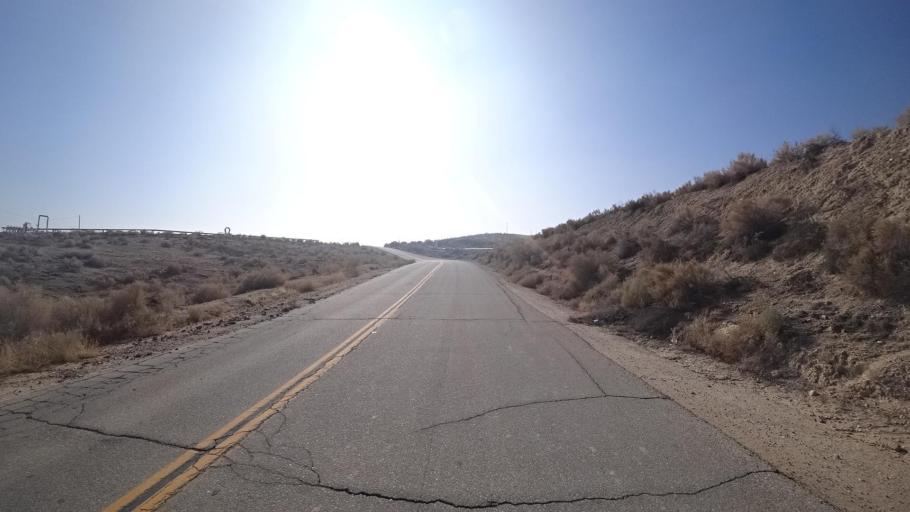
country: US
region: California
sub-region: Kern County
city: Taft Heights
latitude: 35.1423
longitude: -119.5056
